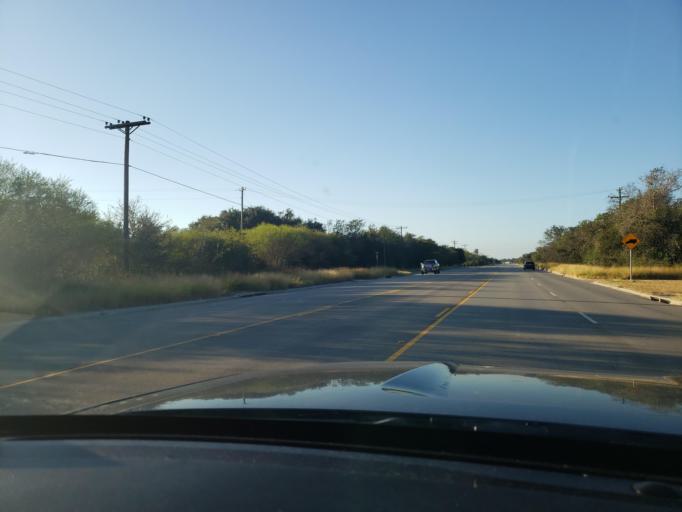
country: US
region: Texas
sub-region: Bee County
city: Beeville
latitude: 28.4333
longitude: -97.7141
